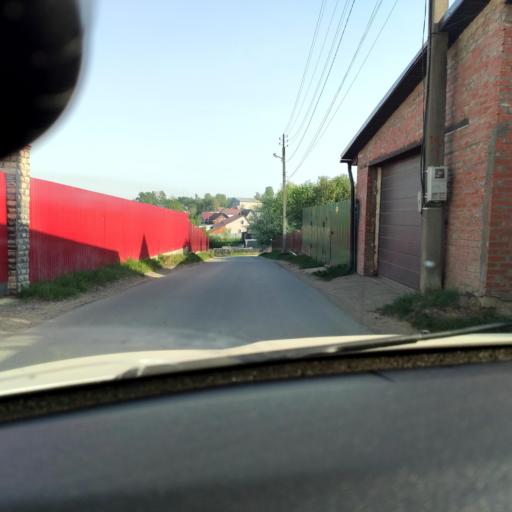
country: RU
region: Perm
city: Polazna
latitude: 58.2998
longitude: 56.4085
